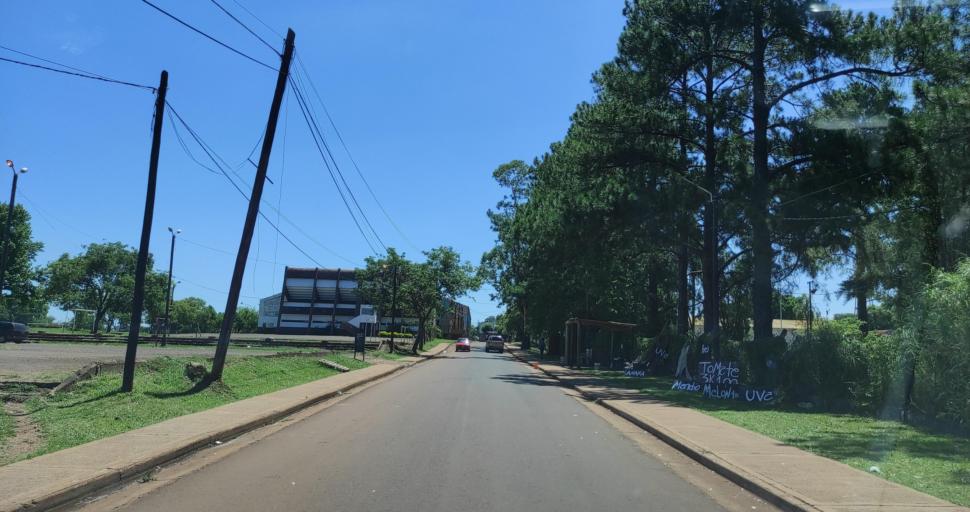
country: AR
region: Misiones
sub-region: Departamento de Capital
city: Posadas
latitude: -27.4167
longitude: -55.9021
